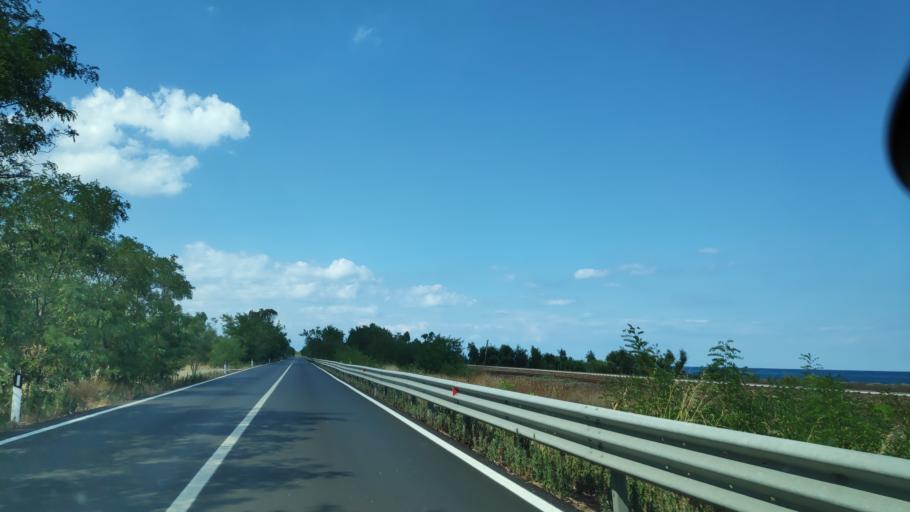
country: IT
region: Calabria
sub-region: Provincia di Catanzaro
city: Santa Caterina dello Ionio Marina
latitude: 38.5479
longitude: 16.5701
